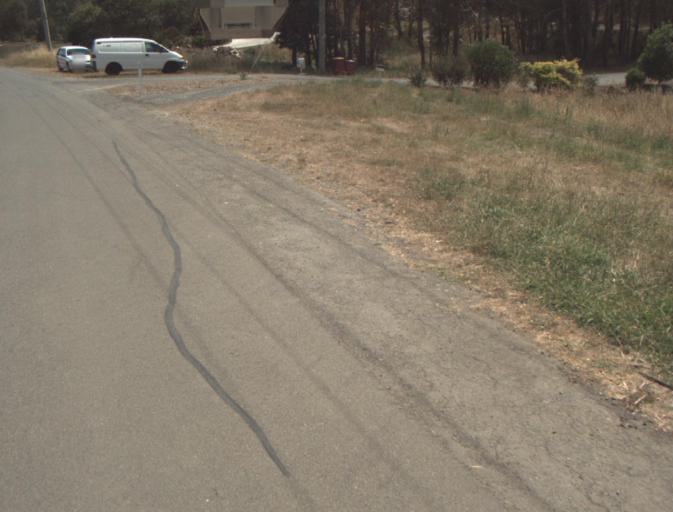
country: AU
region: Tasmania
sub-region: Launceston
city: Summerhill
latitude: -41.4622
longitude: 147.1234
